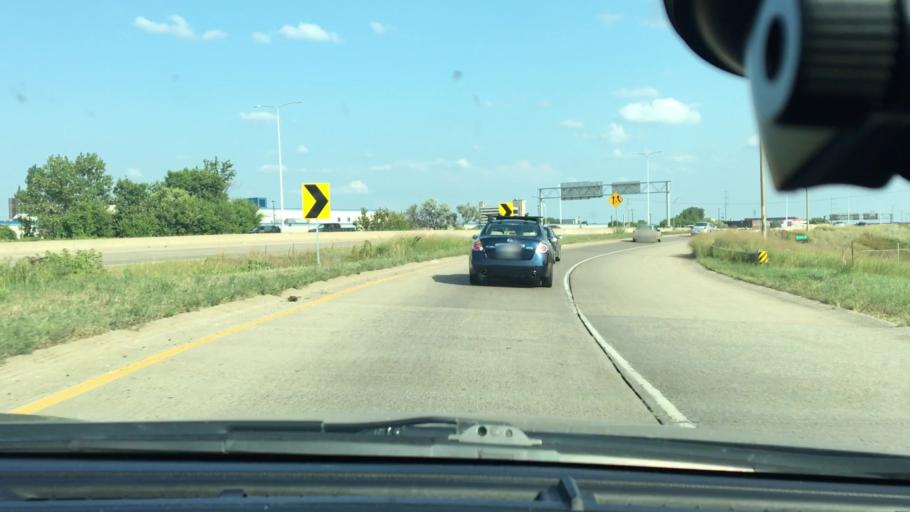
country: US
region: Minnesota
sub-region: Hennepin County
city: Minneapolis
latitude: 44.9652
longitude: -93.2523
